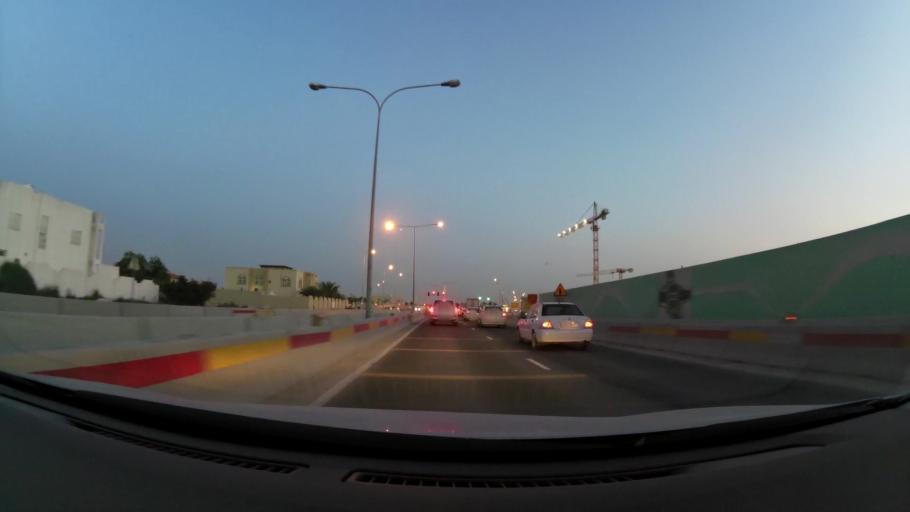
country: QA
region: Baladiyat ar Rayyan
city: Ar Rayyan
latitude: 25.3111
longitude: 51.4531
